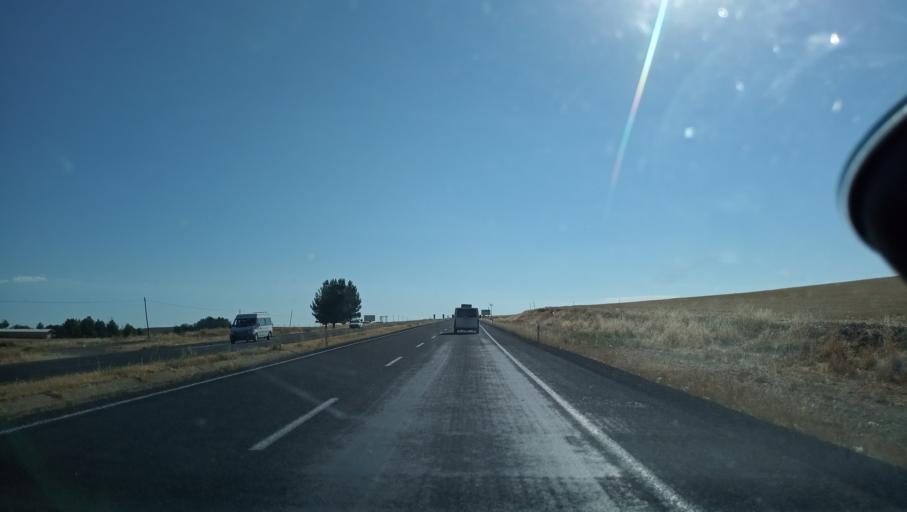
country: TR
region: Diyarbakir
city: Ambar
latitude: 37.9966
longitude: 40.4080
